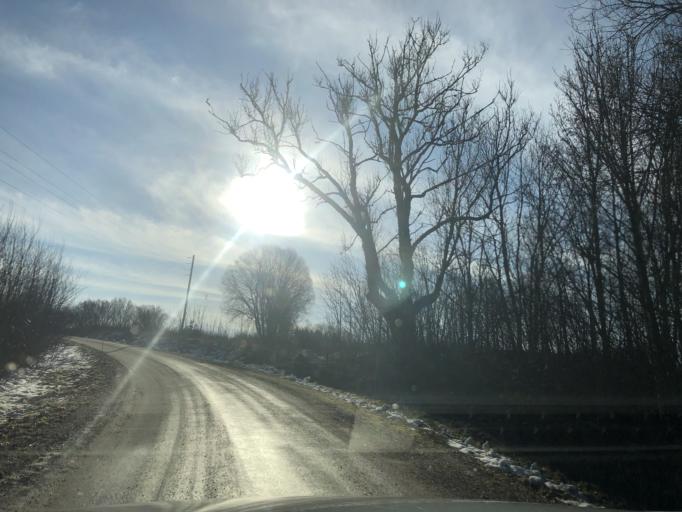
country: SE
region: Vaestra Goetaland
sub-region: Ulricehamns Kommun
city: Ulricehamn
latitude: 57.7966
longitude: 13.4470
